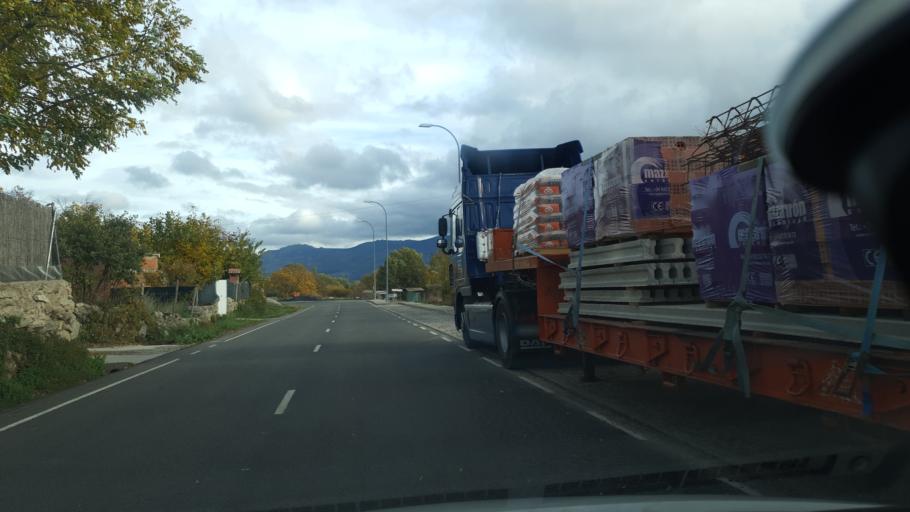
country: ES
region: Castille and Leon
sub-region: Provincia de Avila
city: Hoyocasero
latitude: 40.3976
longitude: -4.9752
